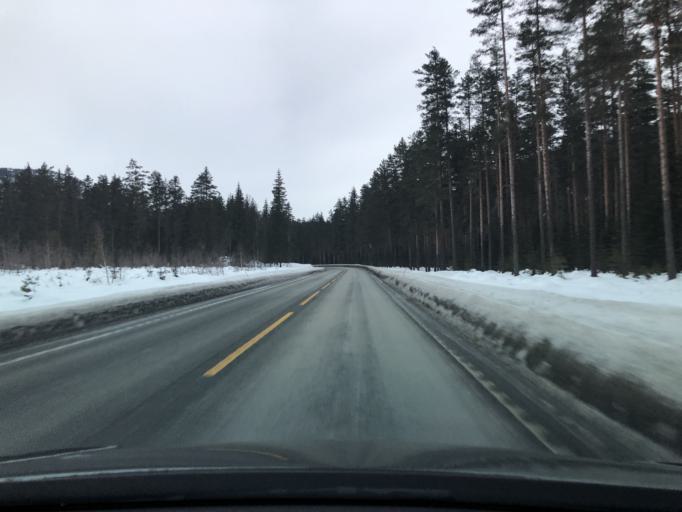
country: NO
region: Oppland
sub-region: Etnedal
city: Bruflat
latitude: 60.6896
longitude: 9.7416
